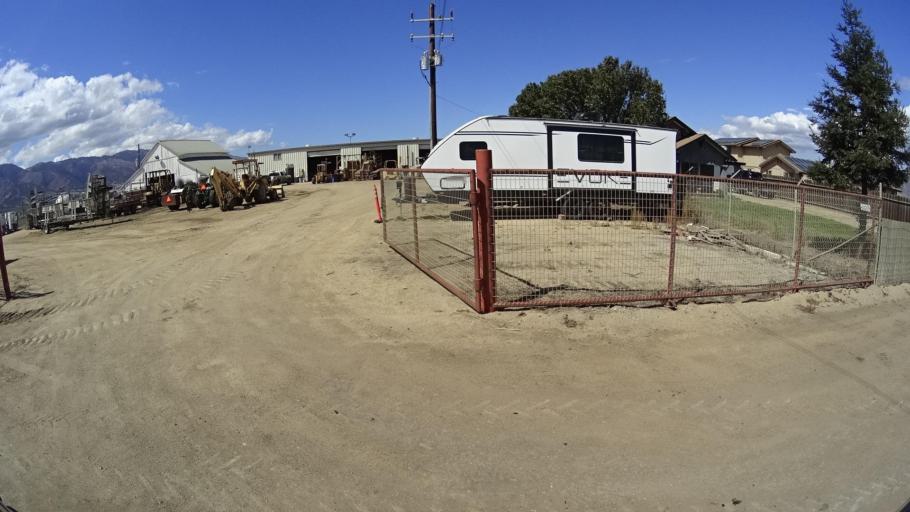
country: US
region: California
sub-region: Monterey County
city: Gonzales
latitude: 36.5084
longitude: -121.4753
